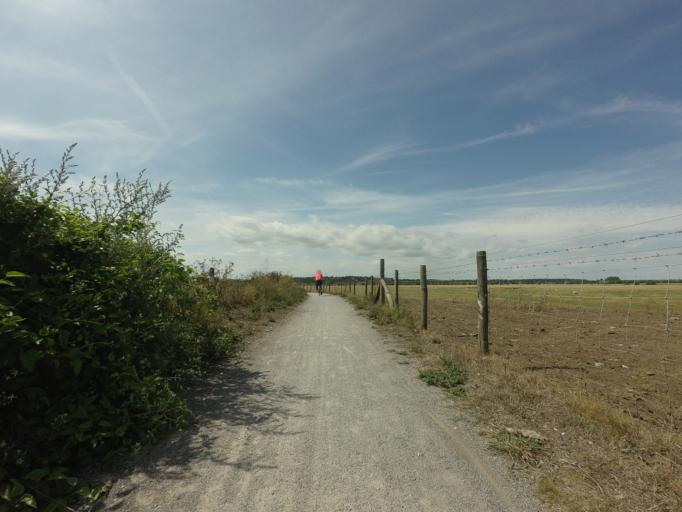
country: GB
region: England
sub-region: East Sussex
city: Rye
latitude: 50.9464
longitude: 0.7594
